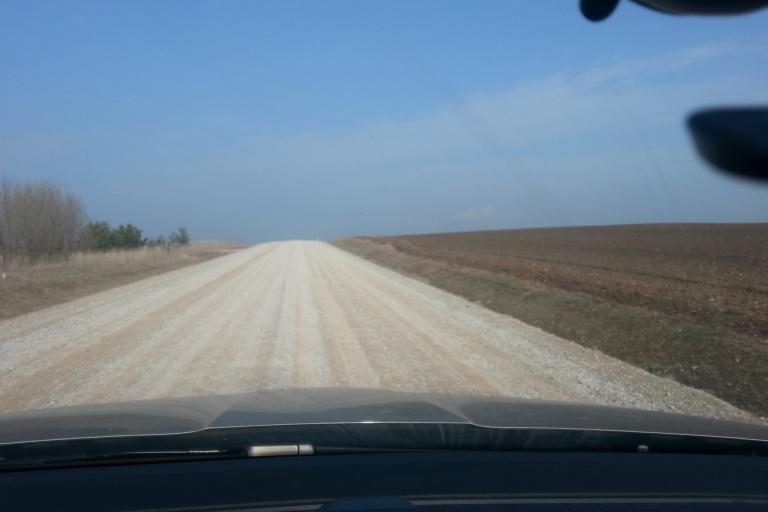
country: LT
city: Trakai
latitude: 54.5905
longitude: 24.9773
